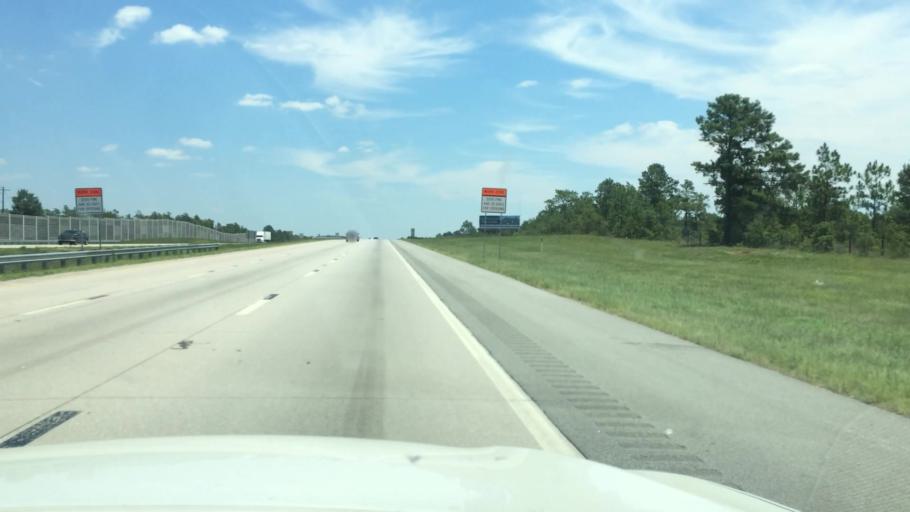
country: US
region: South Carolina
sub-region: Kershaw County
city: Elgin
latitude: 34.0983
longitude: -80.8468
